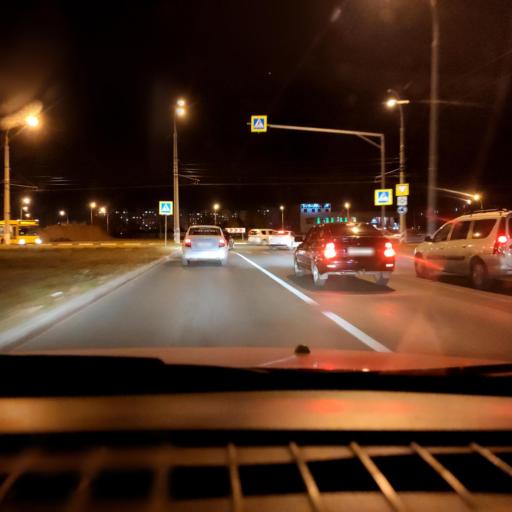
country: RU
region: Samara
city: Tol'yatti
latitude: 53.5250
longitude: 49.3248
